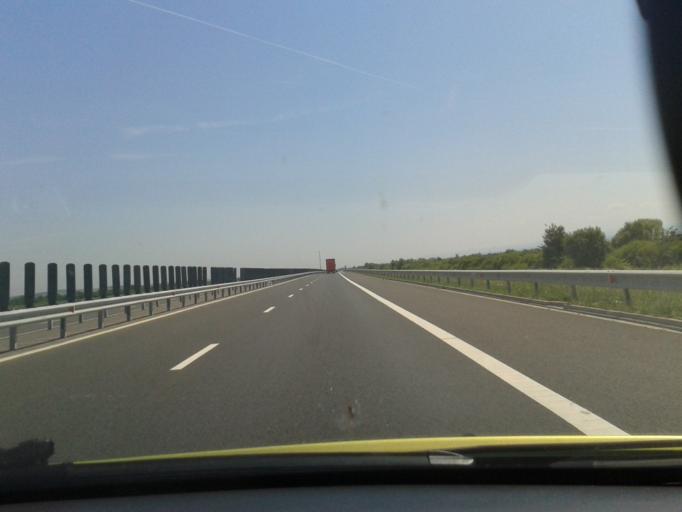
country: RO
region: Timis
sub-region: Comuna Balint
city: Balint
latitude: 45.8051
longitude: 21.9059
